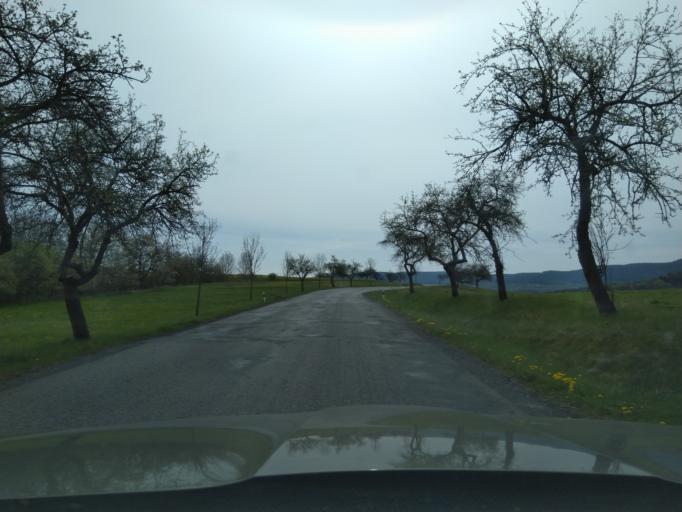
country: CZ
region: Plzensky
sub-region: Okres Klatovy
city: Kasperske Hory
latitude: 49.2033
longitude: 13.6123
